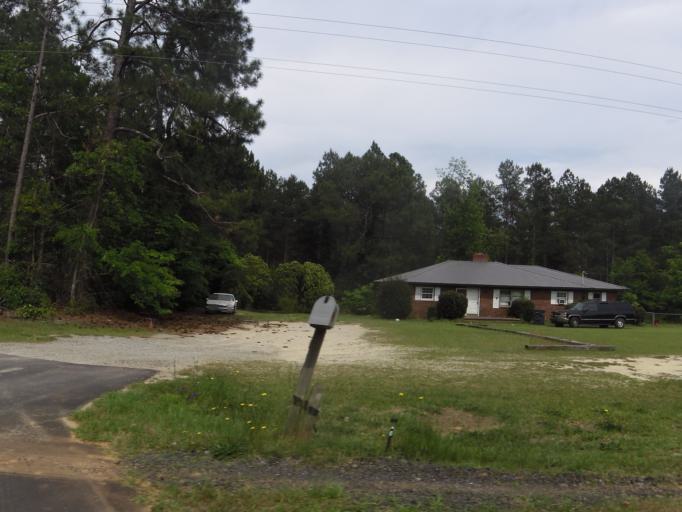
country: US
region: Georgia
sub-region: McDuffie County
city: Thomson
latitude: 33.3889
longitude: -82.4738
